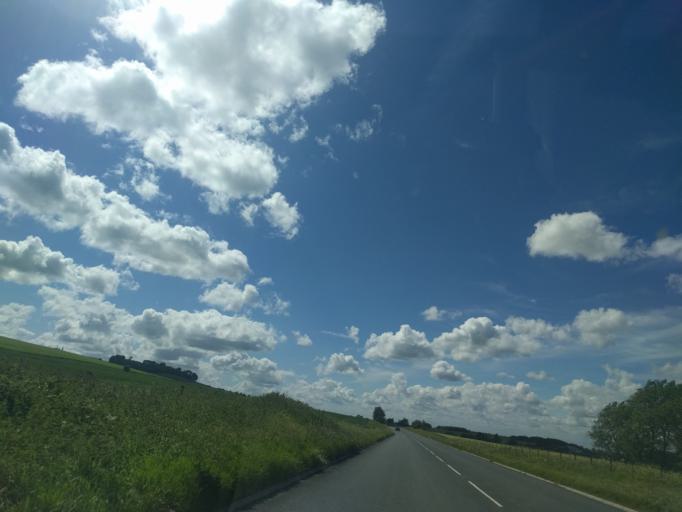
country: GB
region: England
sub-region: Wiltshire
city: Avebury
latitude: 51.4285
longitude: -1.9053
